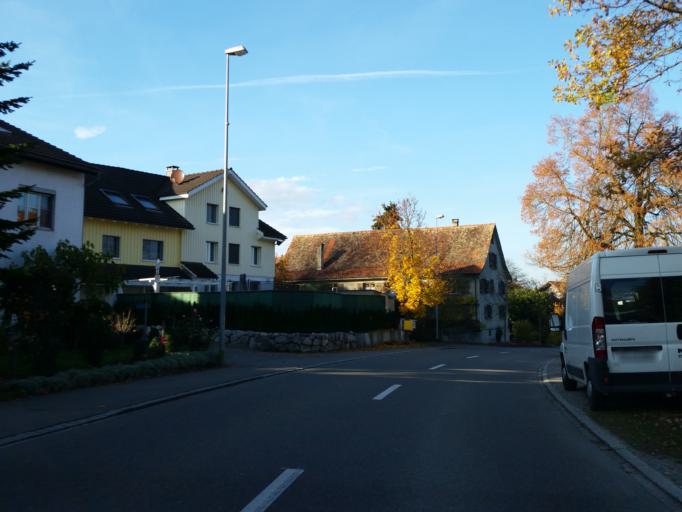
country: CH
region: Thurgau
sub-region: Arbon District
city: Uttwil
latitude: 47.5914
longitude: 9.3155
